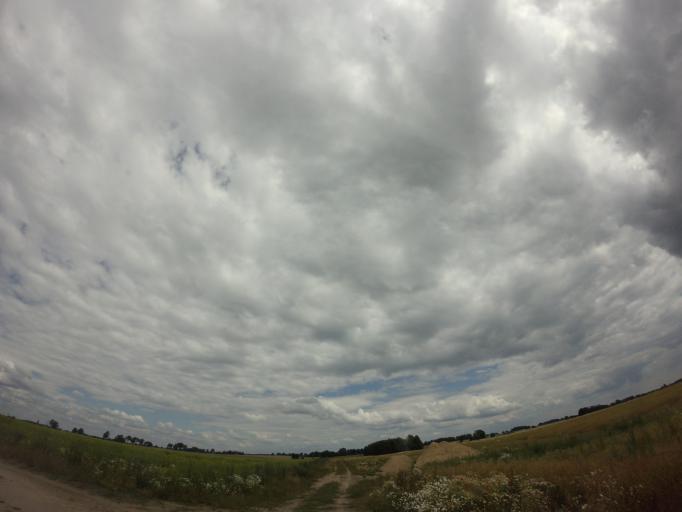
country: PL
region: West Pomeranian Voivodeship
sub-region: Powiat choszczenski
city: Recz
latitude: 53.1817
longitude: 15.5644
